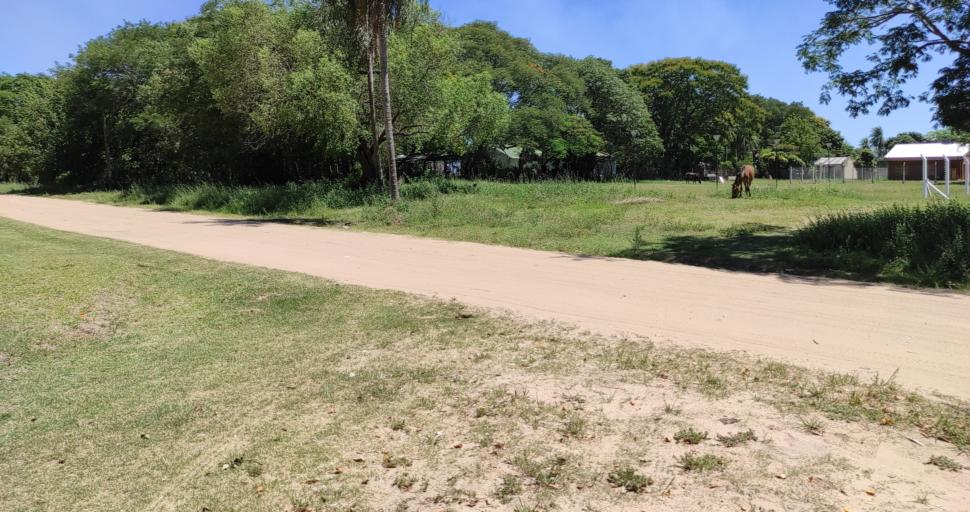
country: AR
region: Corrientes
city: Ituzaingo
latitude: -27.5893
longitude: -56.6998
